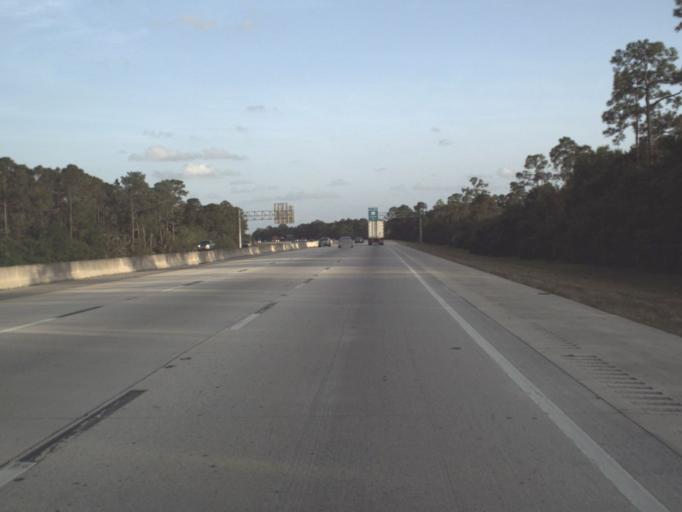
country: US
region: Florida
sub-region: Brevard County
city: Cocoa West
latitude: 28.3930
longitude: -80.8156
